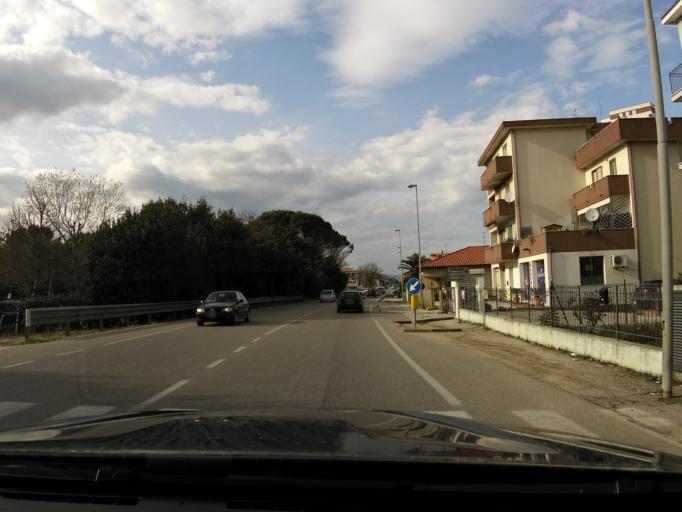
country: IT
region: The Marches
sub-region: Provincia di Macerata
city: Porto Potenza Picena
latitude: 43.3486
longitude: 13.7018
